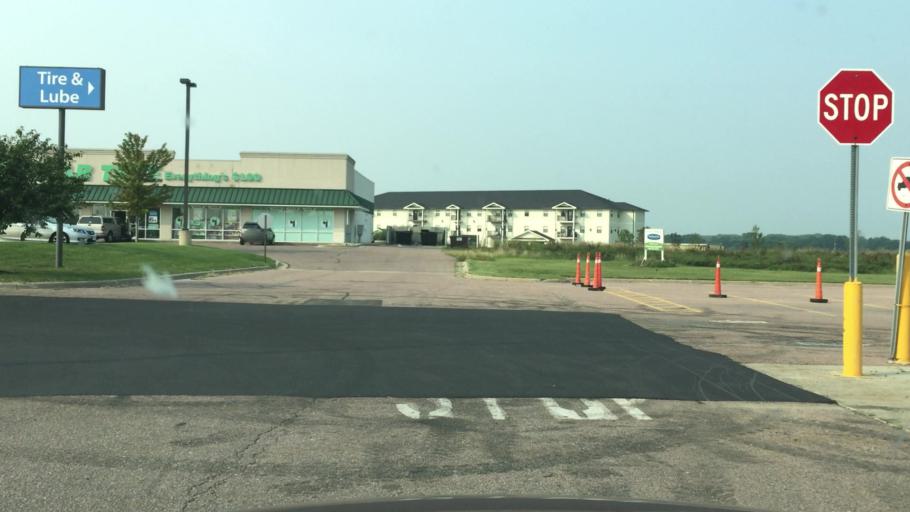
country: US
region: Iowa
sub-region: Plymouth County
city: Le Mars
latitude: 42.7809
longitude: -96.1876
